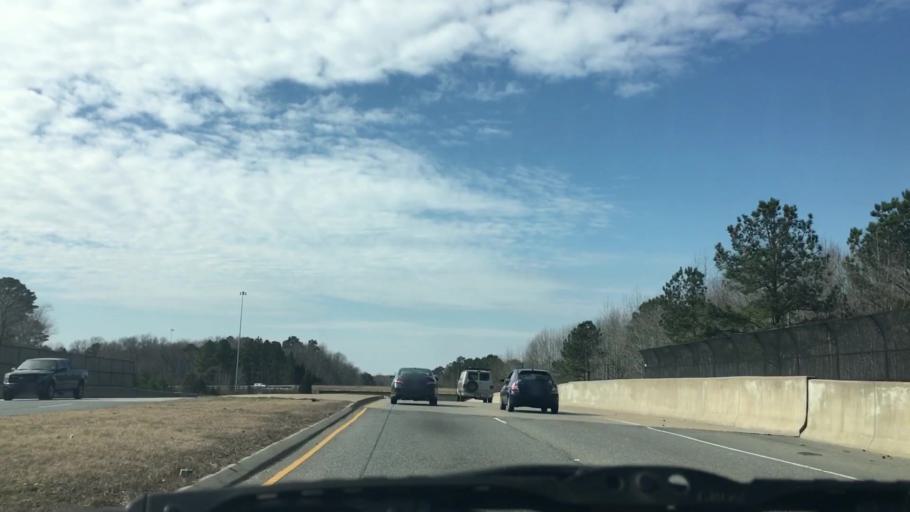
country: US
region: Virginia
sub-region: City of Portsmouth
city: Portsmouth Heights
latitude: 36.8654
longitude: -76.4271
